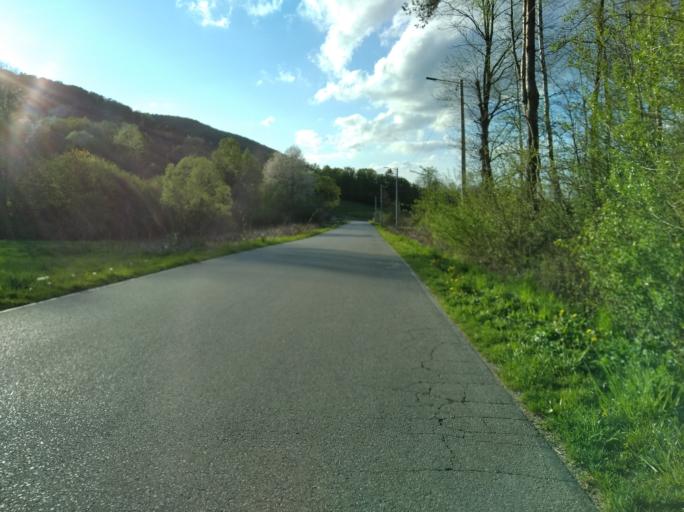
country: PL
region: Subcarpathian Voivodeship
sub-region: Powiat krosnienski
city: Odrzykon
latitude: 49.7854
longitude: 21.7602
